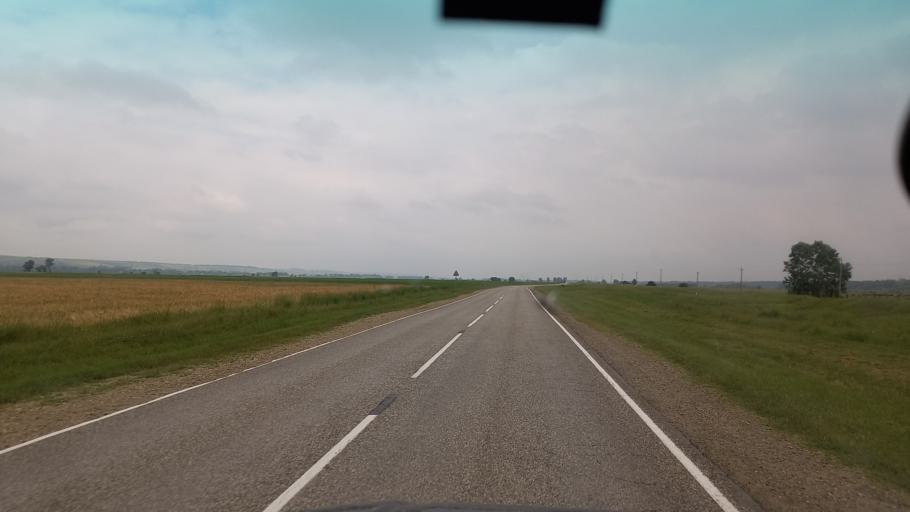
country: RU
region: Adygeya
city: Khodz'
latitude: 44.4850
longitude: 40.7528
